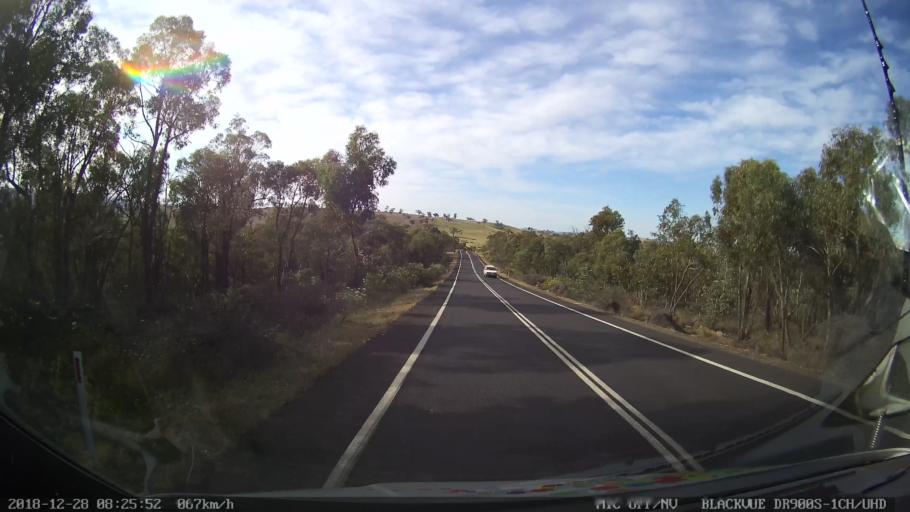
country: AU
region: New South Wales
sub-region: Blayney
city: Blayney
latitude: -33.9300
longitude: 149.3501
